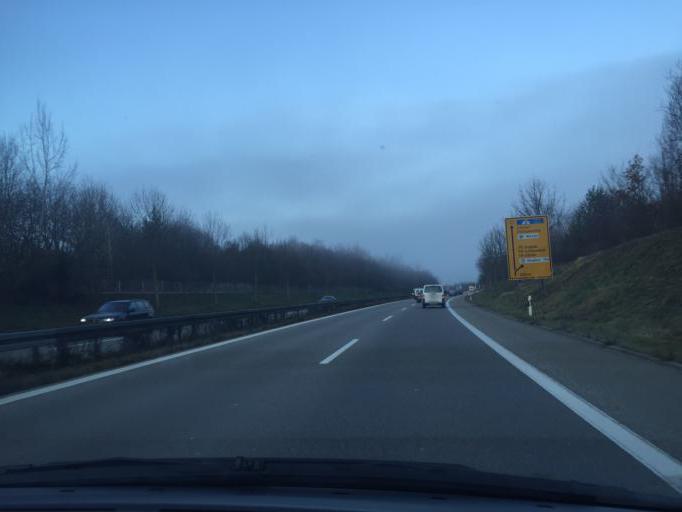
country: DE
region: Baden-Wuerttemberg
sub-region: Freiburg Region
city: Kirchzarten
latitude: 47.9756
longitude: 7.9203
